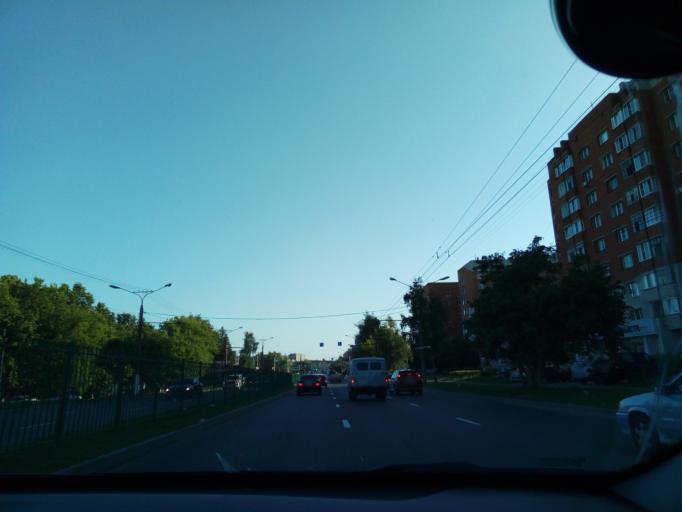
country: RU
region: Chuvashia
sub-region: Cheboksarskiy Rayon
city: Cheboksary
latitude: 56.1142
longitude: 47.2719
